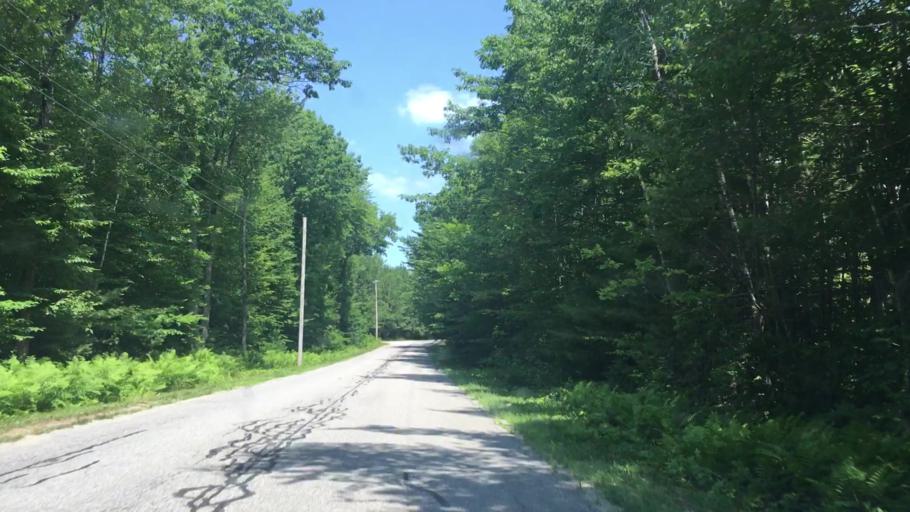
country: US
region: Maine
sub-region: Kennebec County
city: Wayne
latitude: 44.3175
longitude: -70.0583
